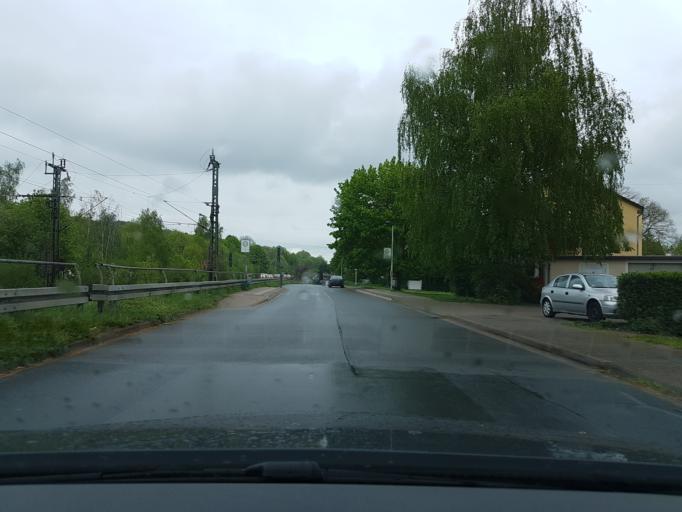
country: DE
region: Lower Saxony
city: Hameln
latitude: 52.1071
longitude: 9.3978
